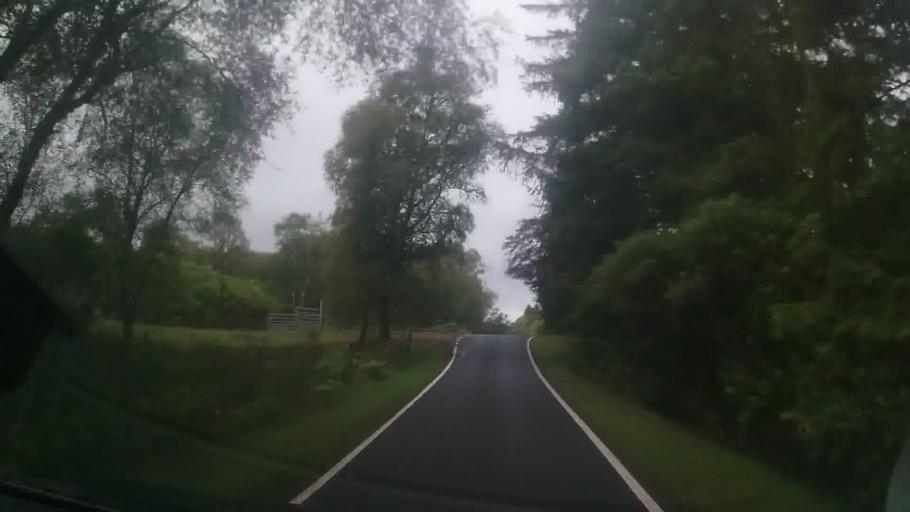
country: GB
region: Scotland
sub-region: Argyll and Bute
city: Isle Of Mull
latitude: 56.6775
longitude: -5.8957
